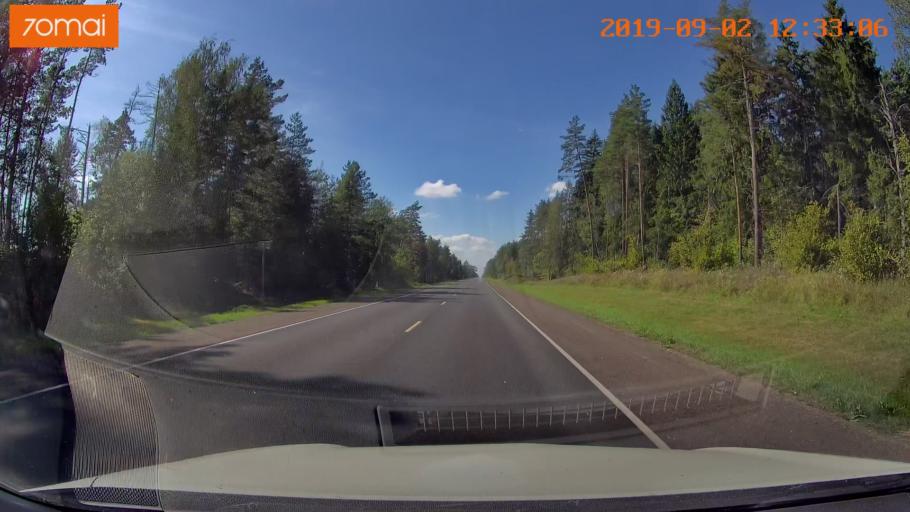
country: RU
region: Smolensk
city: Shumyachi
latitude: 53.8204
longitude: 32.4368
